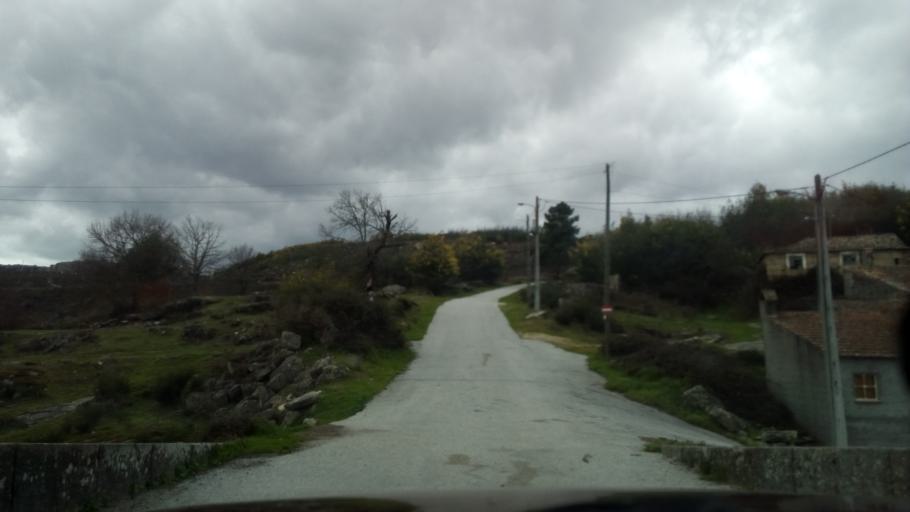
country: PT
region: Guarda
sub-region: Fornos de Algodres
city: Fornos de Algodres
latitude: 40.5860
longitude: -7.5671
